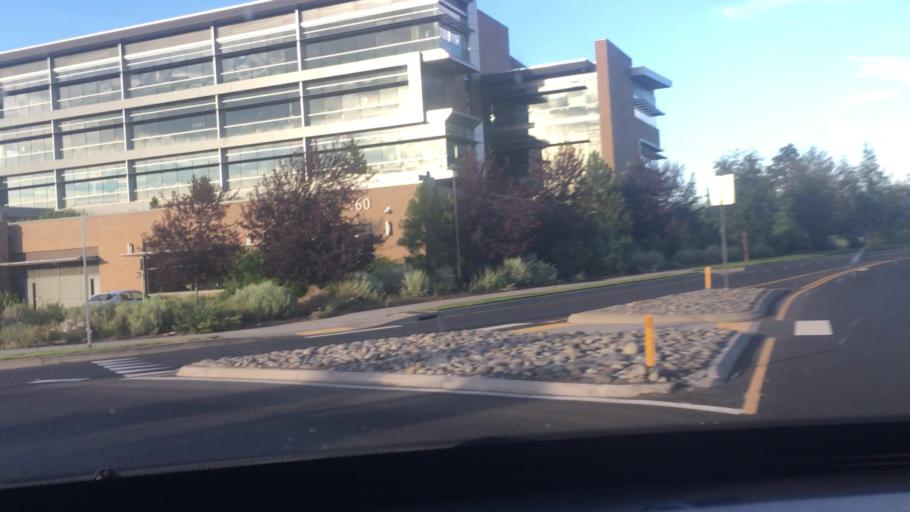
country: US
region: Oregon
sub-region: Deschutes County
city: Bend
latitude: 44.0460
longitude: -121.3096
